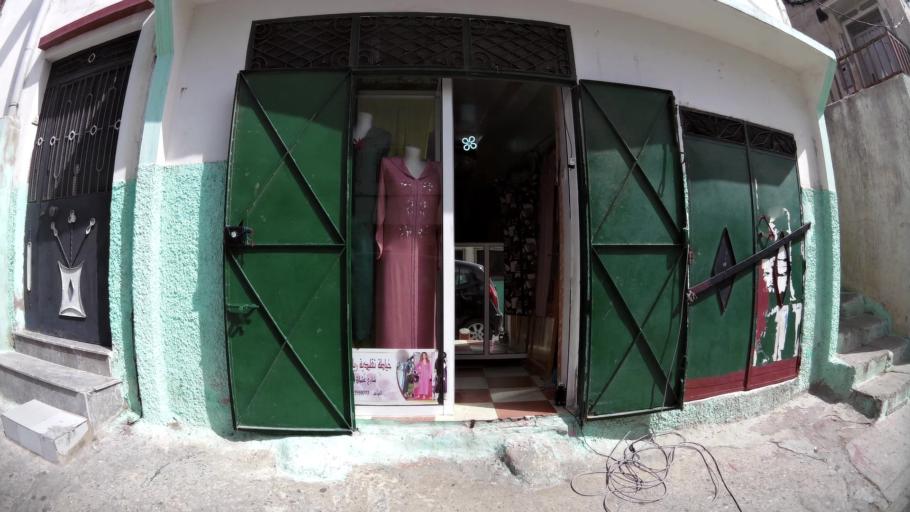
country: MA
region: Tanger-Tetouan
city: Tetouan
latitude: 35.5786
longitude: -5.3849
